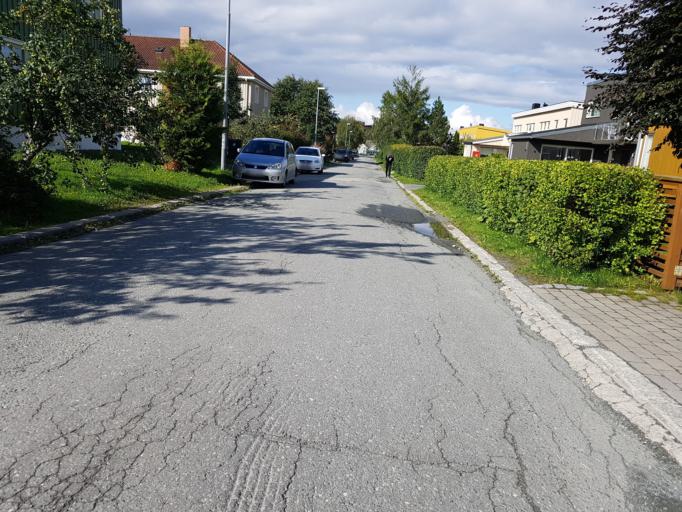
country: NO
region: Sor-Trondelag
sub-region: Trondheim
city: Trondheim
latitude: 63.4254
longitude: 10.4397
